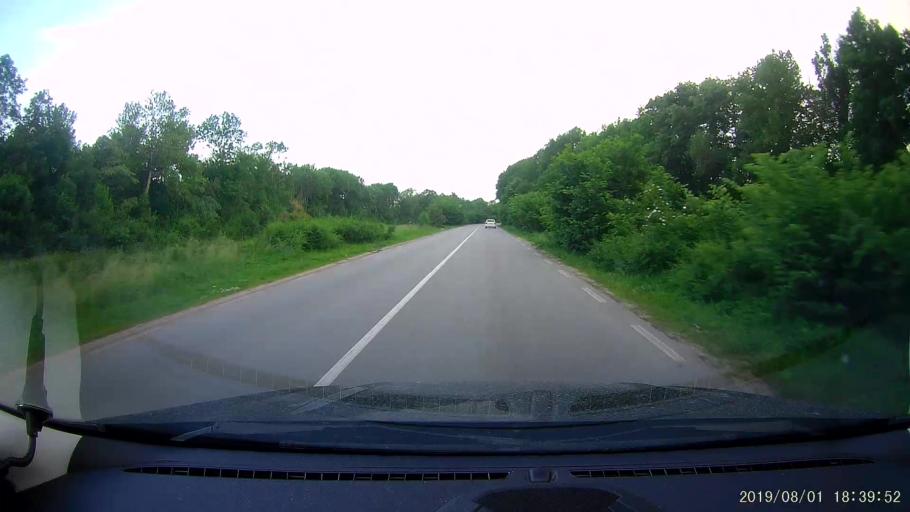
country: BG
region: Shumen
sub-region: Obshtina Khitrino
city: Gara Khitrino
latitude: 43.3769
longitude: 26.9190
